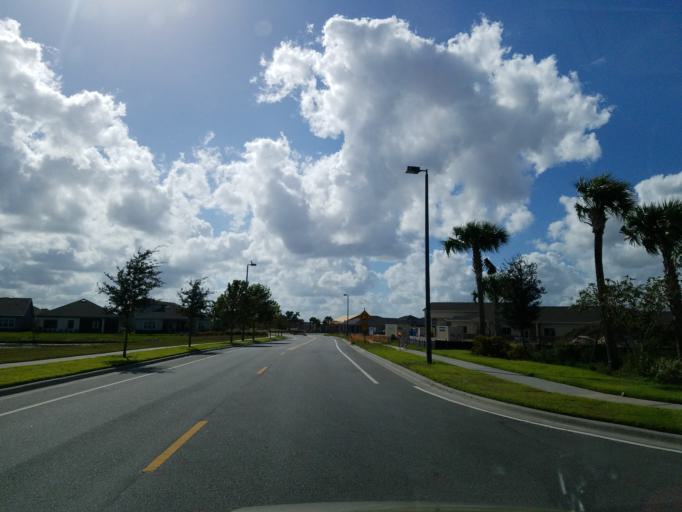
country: US
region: Florida
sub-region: Hillsborough County
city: Apollo Beach
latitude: 27.7713
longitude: -82.3692
